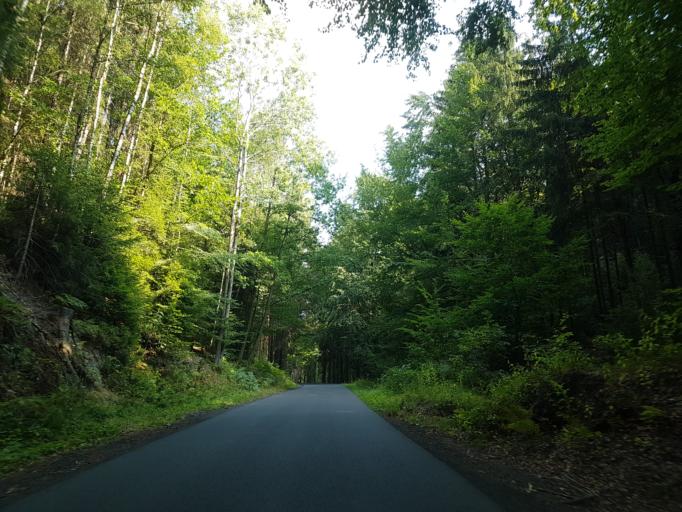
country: CZ
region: Ustecky
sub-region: Okres Decin
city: Decin
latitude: 50.8705
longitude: 14.2492
